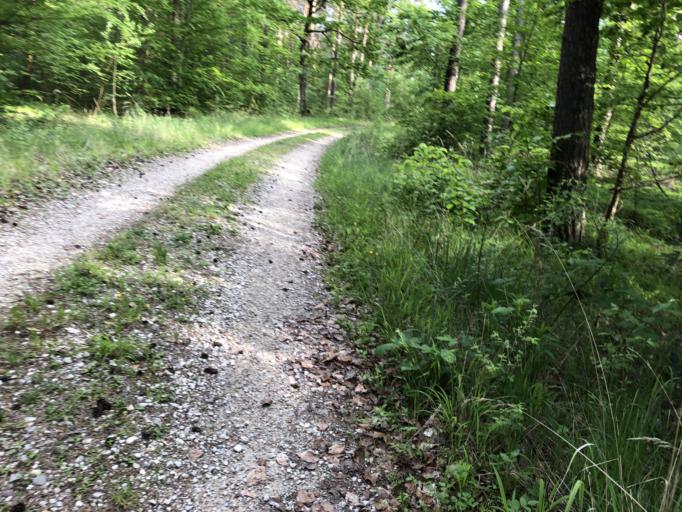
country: DE
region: Bavaria
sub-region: Upper Franconia
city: Memmelsdorf
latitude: 49.9199
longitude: 10.9543
